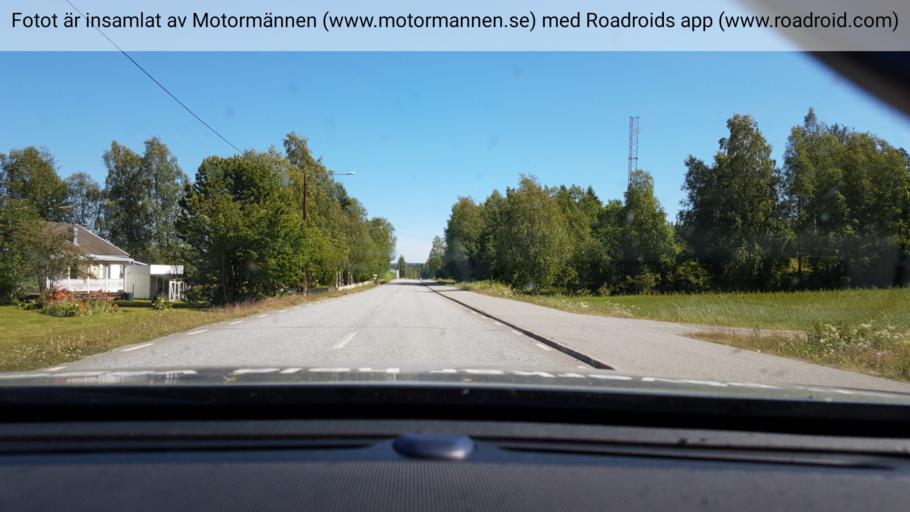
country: SE
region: Vaesterbotten
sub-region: Vilhelmina Kommun
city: Sjoberg
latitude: 64.6378
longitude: 16.3658
